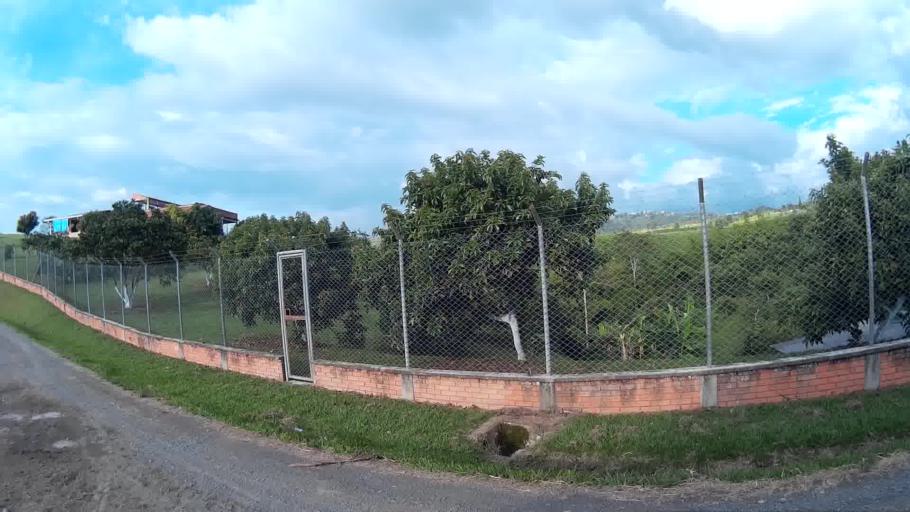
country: CO
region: Valle del Cauca
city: Ulloa
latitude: 4.7403
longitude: -75.7390
